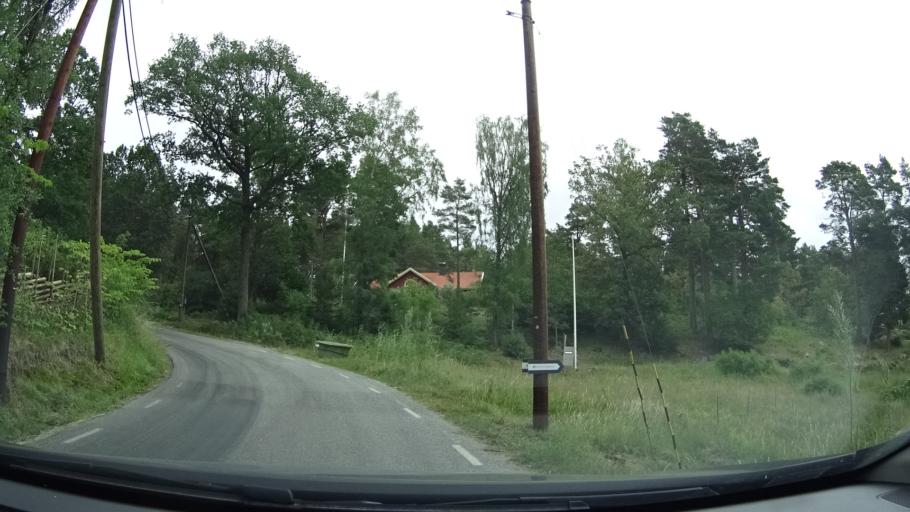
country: SE
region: Stockholm
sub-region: Varmdo Kommun
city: Mortnas
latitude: 59.3718
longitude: 18.4670
